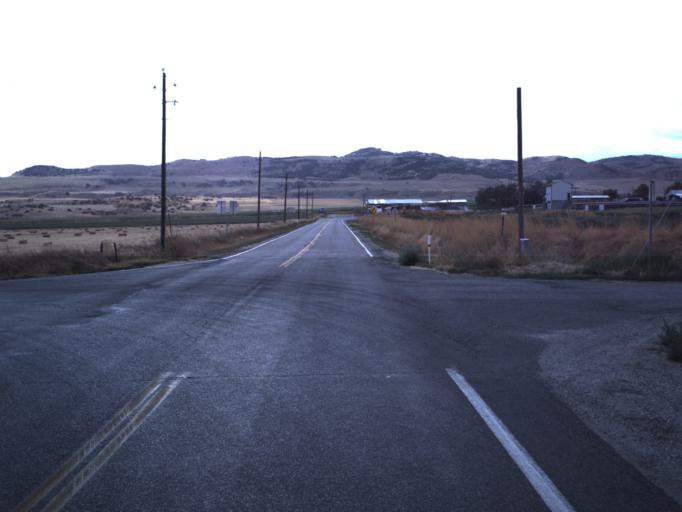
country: US
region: Utah
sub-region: Cache County
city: Benson
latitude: 41.8626
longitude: -111.9995
